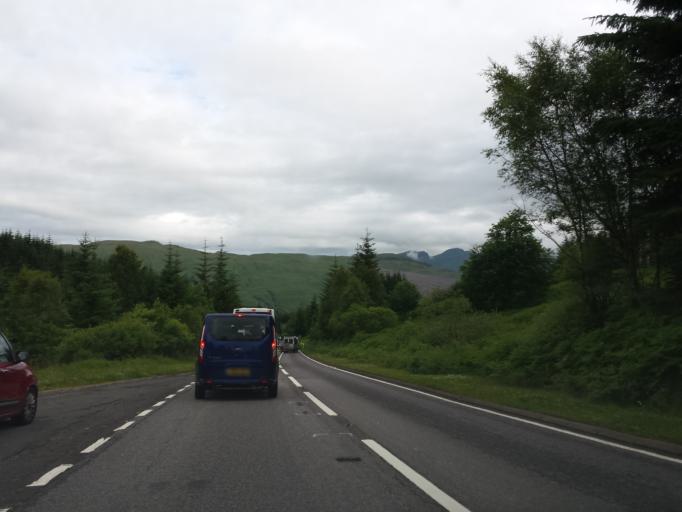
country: GB
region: Scotland
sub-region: Stirling
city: Callander
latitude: 56.4314
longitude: -4.3411
